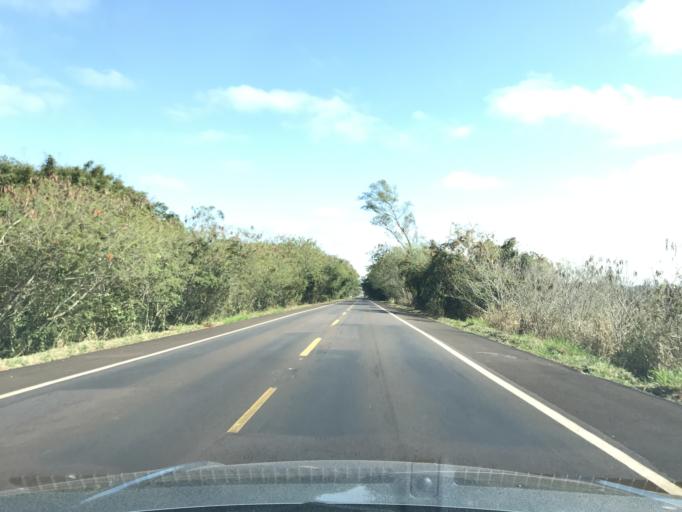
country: BR
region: Parana
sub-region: Altonia
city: Altania
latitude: -24.0741
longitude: -53.9811
